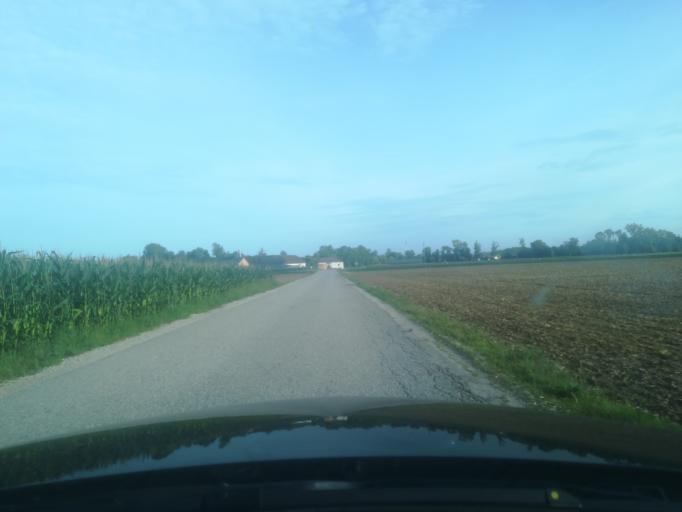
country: AT
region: Upper Austria
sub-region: Wels-Land
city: Marchtrenk
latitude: 48.1768
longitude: 14.1591
